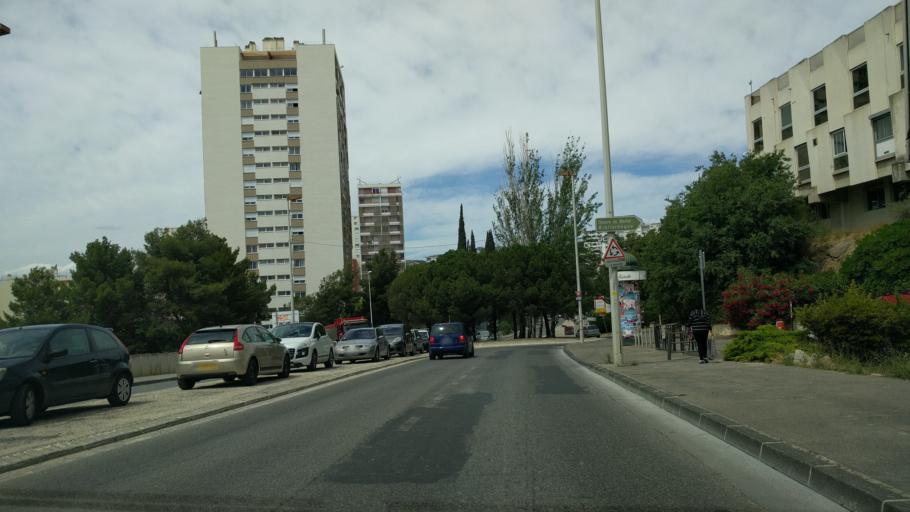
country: FR
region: Provence-Alpes-Cote d'Azur
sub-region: Departement des Bouches-du-Rhone
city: Marseille 13
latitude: 43.3305
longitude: 5.3983
